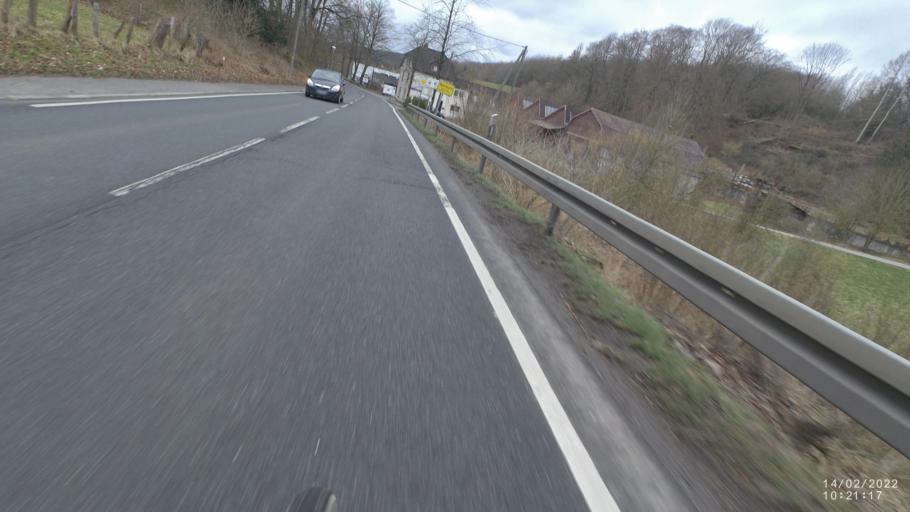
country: DE
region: North Rhine-Westphalia
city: Balve
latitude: 51.3608
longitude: 7.9045
